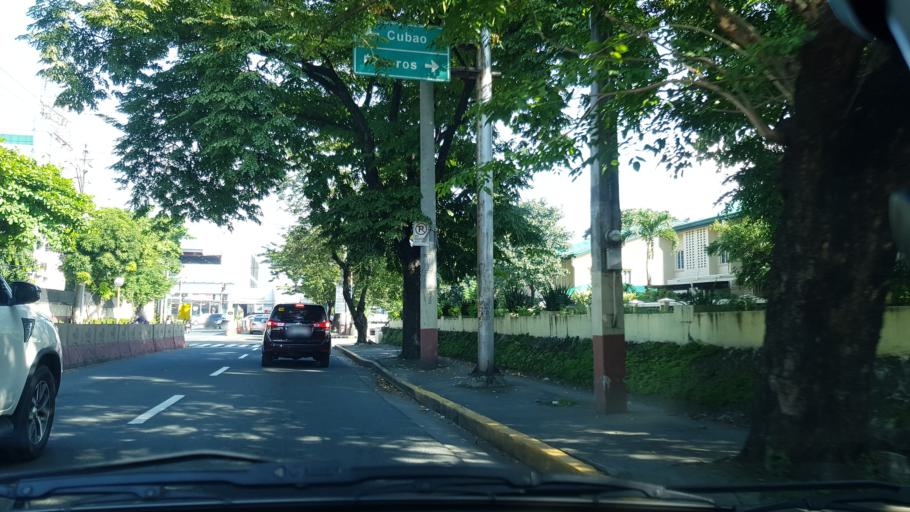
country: PH
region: Metro Manila
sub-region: Pasig
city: Pasig City
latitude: 14.5782
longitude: 121.0725
